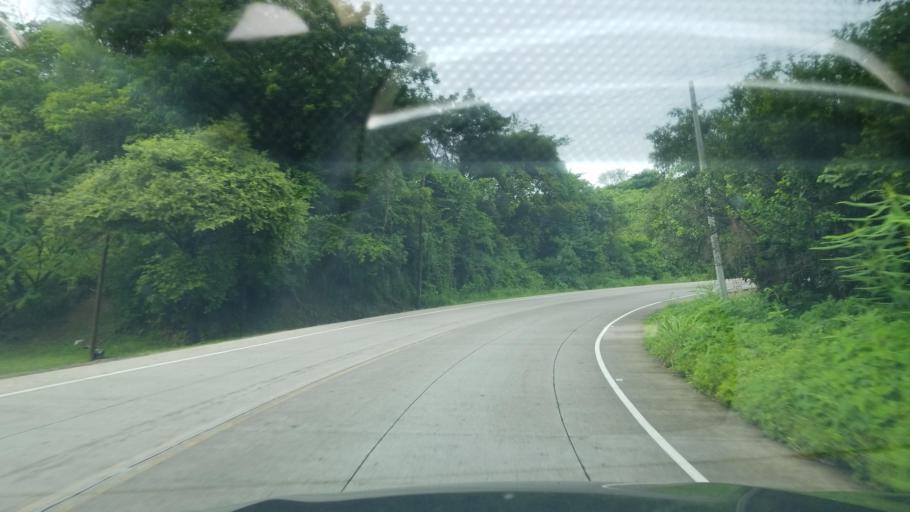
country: HN
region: Choluteca
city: Pespire
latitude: 13.6508
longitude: -87.3650
